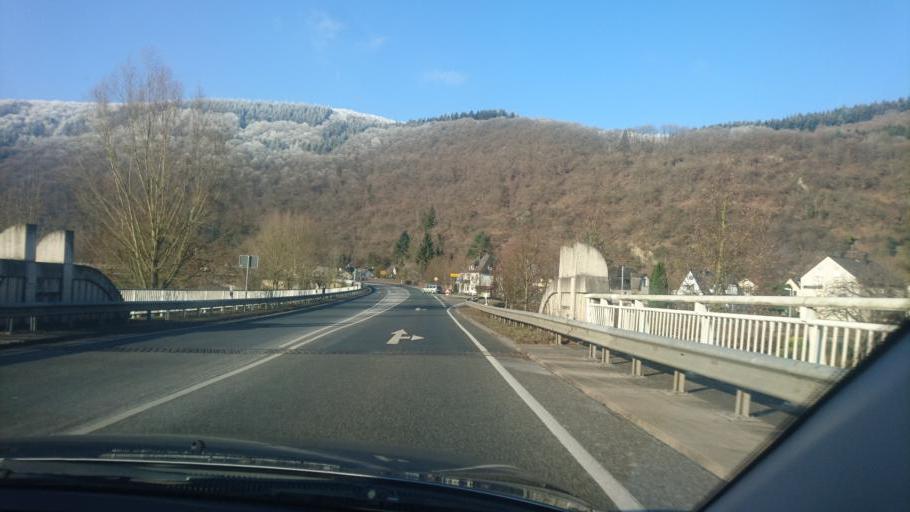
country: DE
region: Rheinland-Pfalz
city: Fachbach
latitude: 50.3381
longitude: 7.6859
